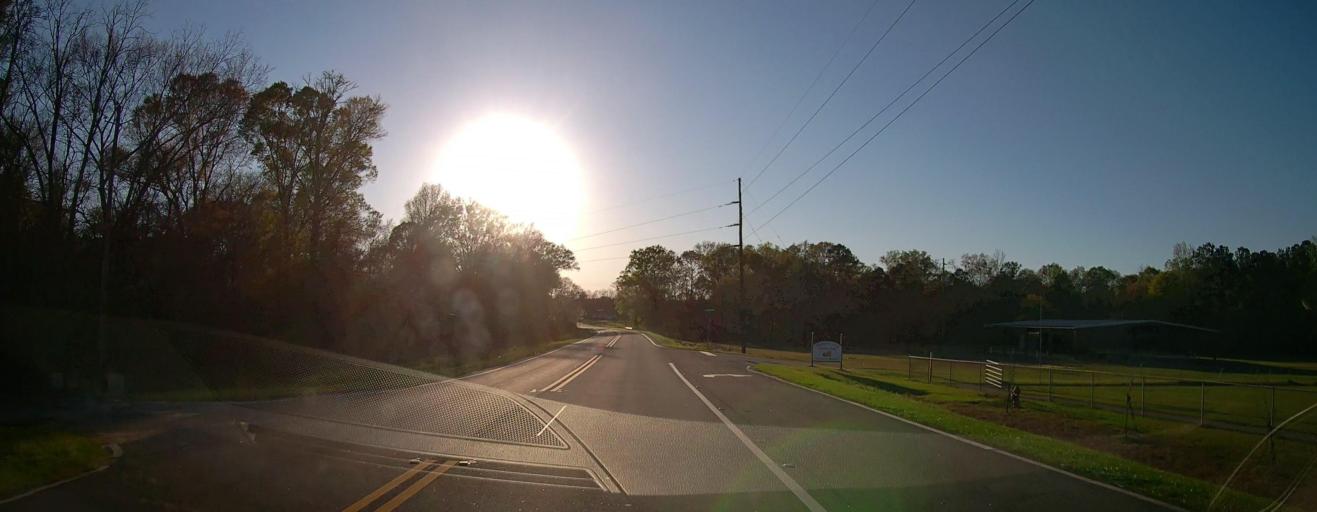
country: US
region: Georgia
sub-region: Wilcox County
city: Abbeville
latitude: 31.9924
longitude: -83.3142
